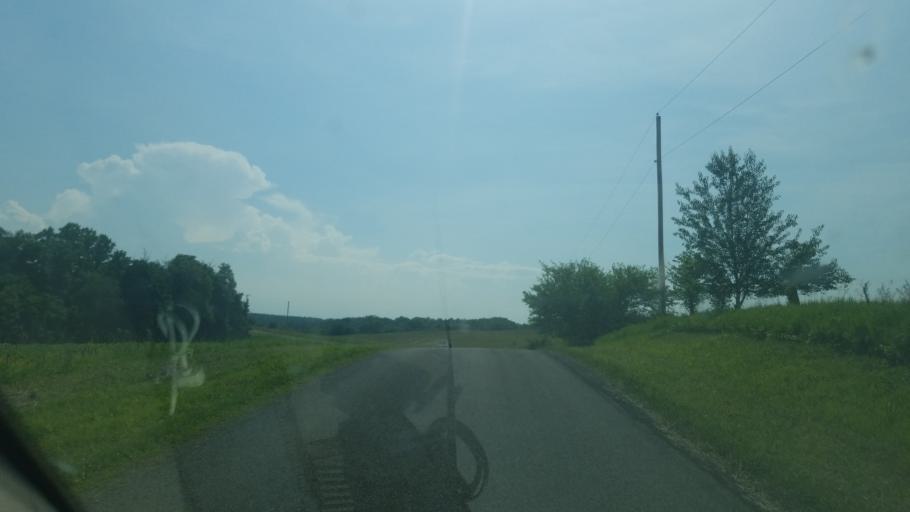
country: US
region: Ohio
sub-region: Champaign County
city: North Lewisburg
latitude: 40.2756
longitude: -83.6495
